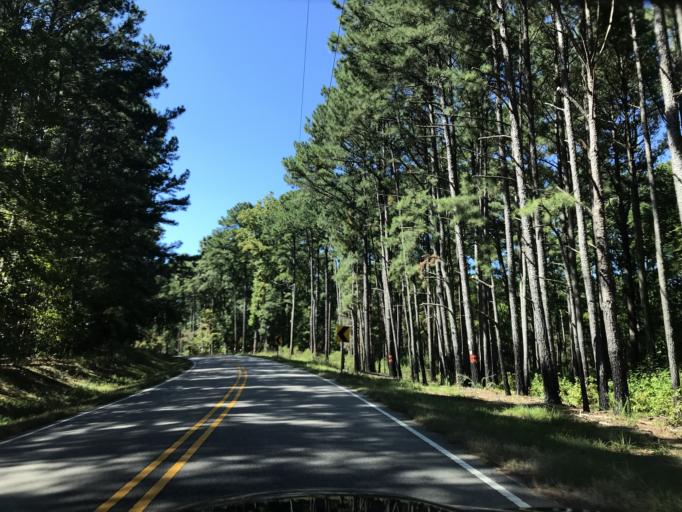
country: US
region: North Carolina
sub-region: Wake County
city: Wake Forest
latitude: 35.9578
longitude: -78.6158
